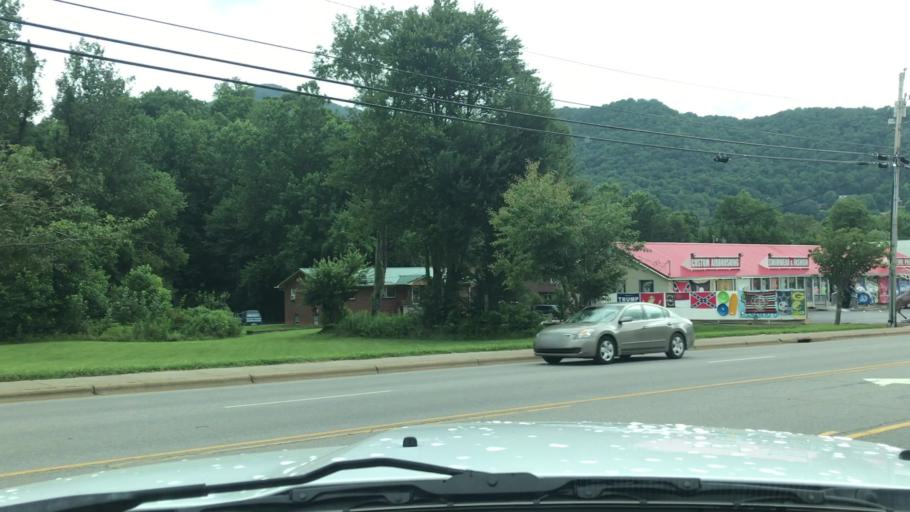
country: US
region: North Carolina
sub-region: Haywood County
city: Maggie Valley
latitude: 35.5176
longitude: -83.0916
